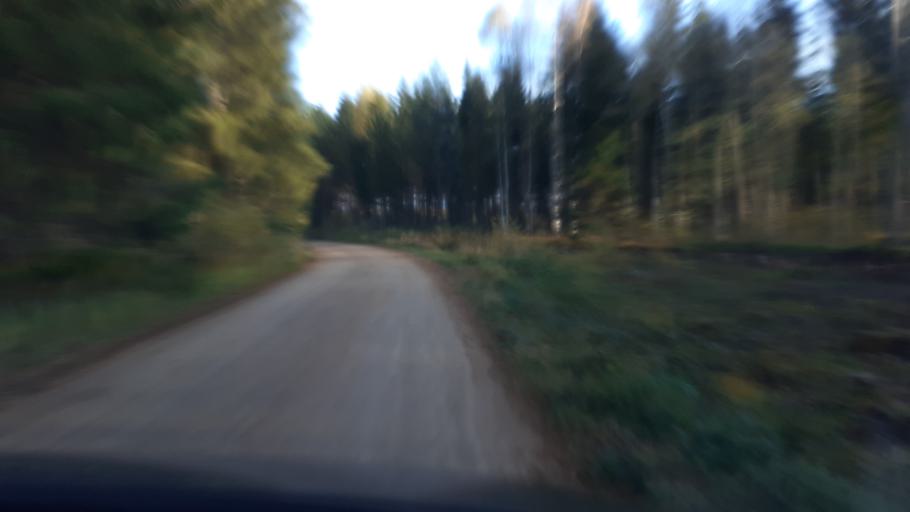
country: LV
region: Kuldigas Rajons
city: Kuldiga
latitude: 56.8565
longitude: 22.1052
